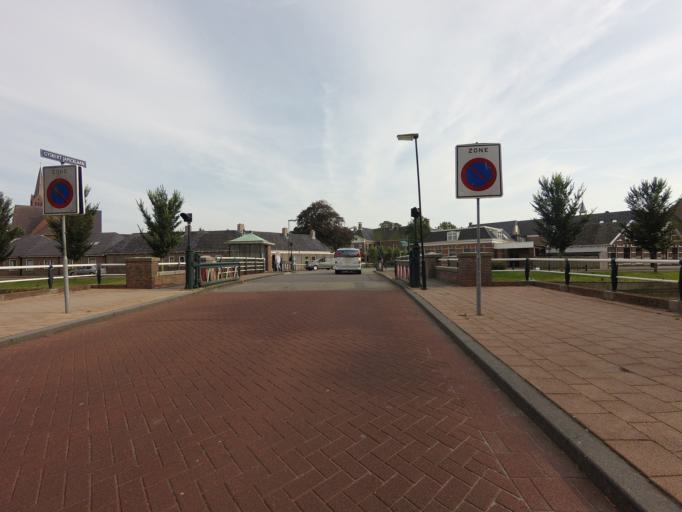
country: NL
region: Friesland
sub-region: Sudwest Fryslan
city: Bolsward
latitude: 53.0636
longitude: 5.5199
